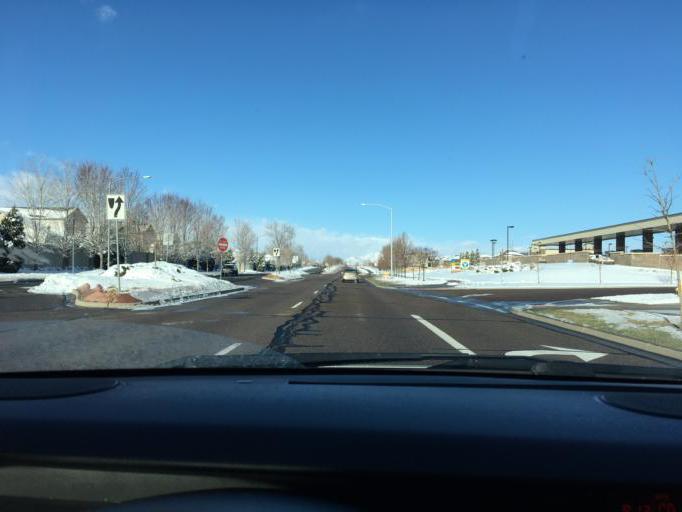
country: US
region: Colorado
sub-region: Adams County
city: Northglenn
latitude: 39.9432
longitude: -104.9985
